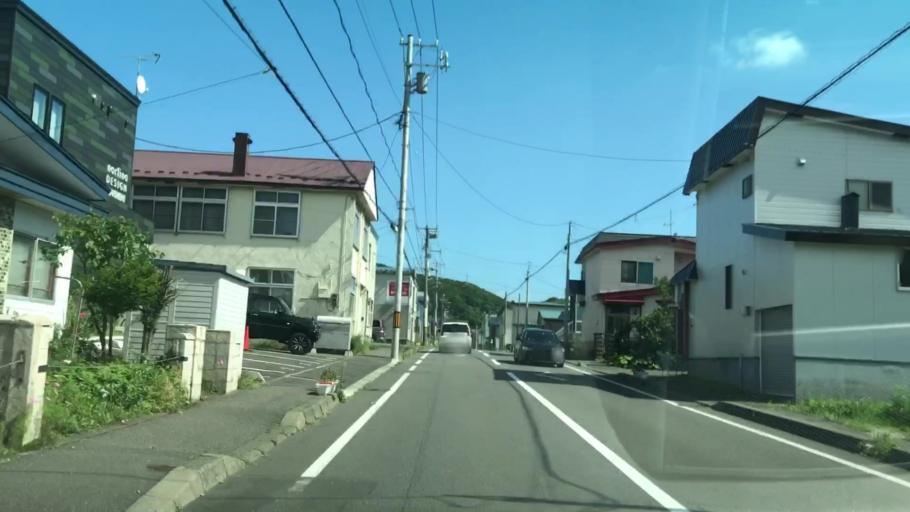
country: JP
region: Hokkaido
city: Muroran
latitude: 42.3122
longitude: 140.9926
